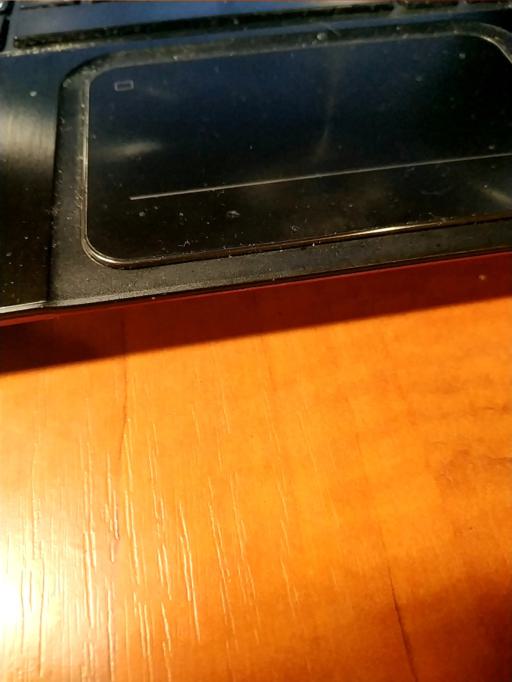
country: RU
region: Tverskaya
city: Rameshki
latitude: 57.2445
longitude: 35.8976
